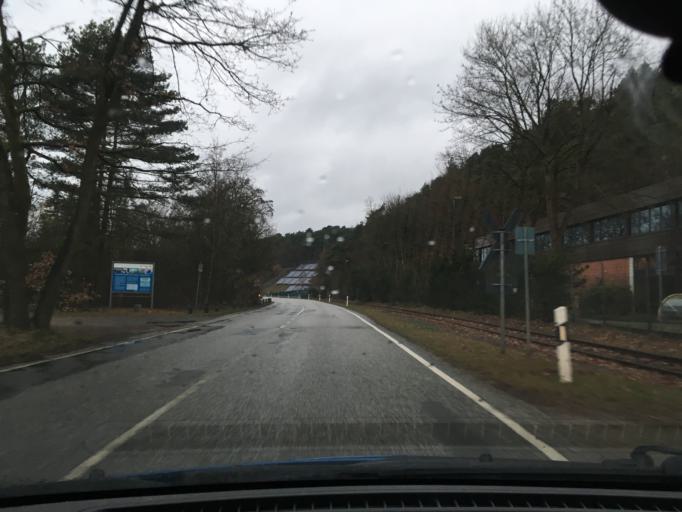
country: DE
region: Lower Saxony
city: Marschacht
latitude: 53.4174
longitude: 10.3968
